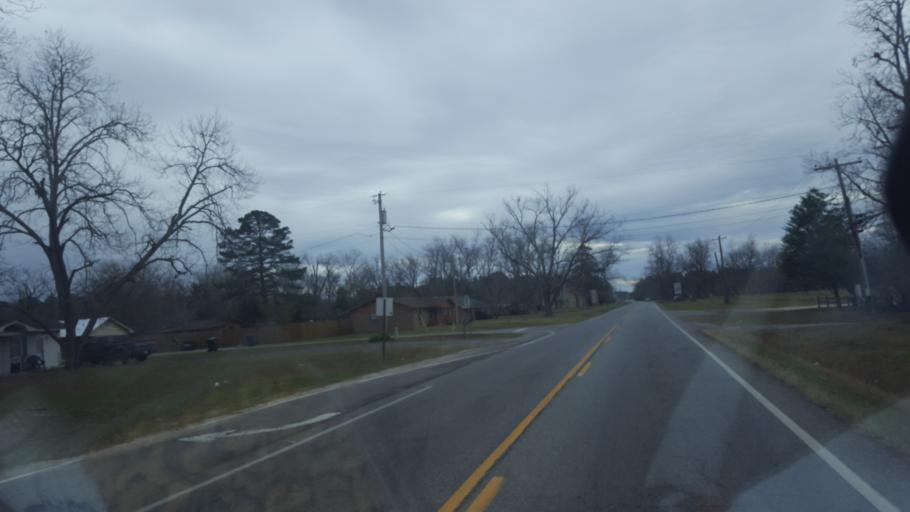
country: US
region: Georgia
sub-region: Ben Hill County
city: Fitzgerald
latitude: 31.7416
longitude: -83.2610
